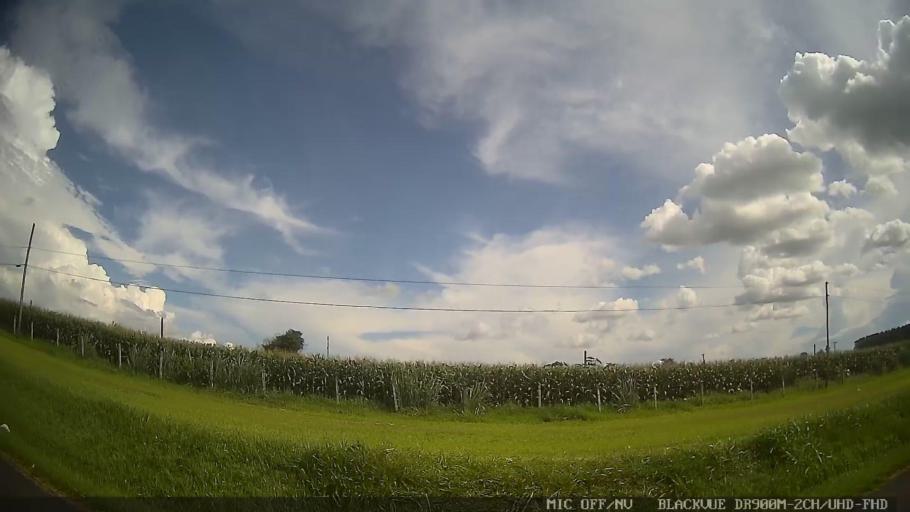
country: BR
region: Sao Paulo
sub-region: Laranjal Paulista
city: Laranjal Paulista
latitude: -23.0396
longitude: -47.8996
